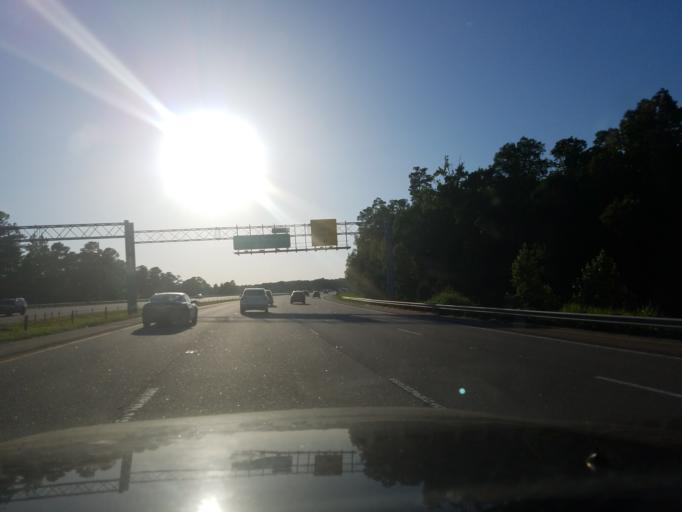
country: US
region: North Carolina
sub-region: Wake County
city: Raleigh
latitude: 35.8770
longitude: -78.5837
